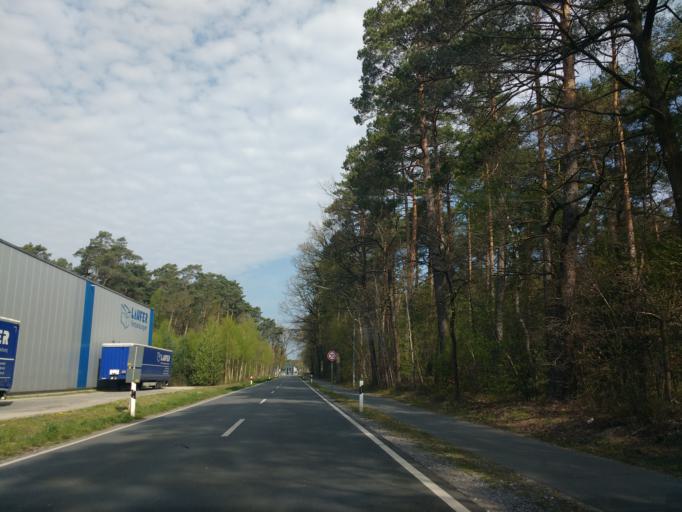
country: DE
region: North Rhine-Westphalia
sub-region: Regierungsbezirk Detmold
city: Hovelhof
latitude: 51.8345
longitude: 8.6555
